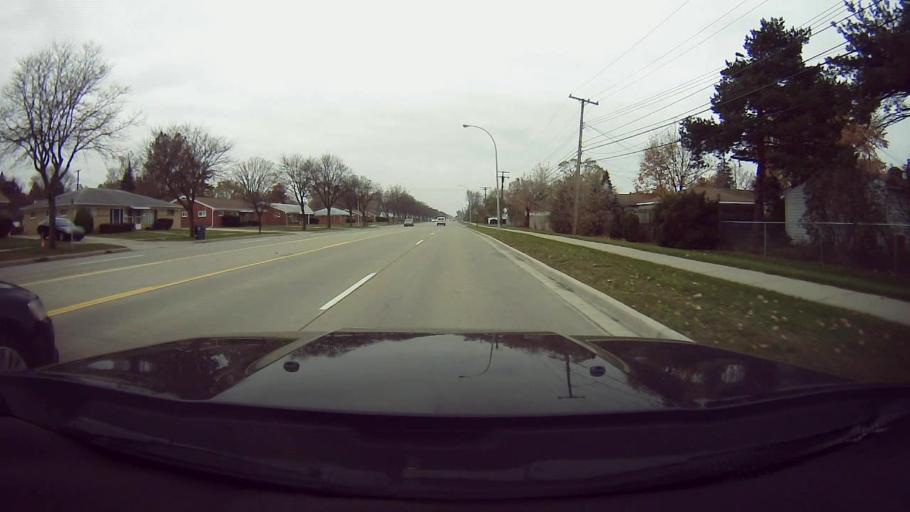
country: US
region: Michigan
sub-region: Oakland County
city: Royal Oak
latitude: 42.5089
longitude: -83.1253
